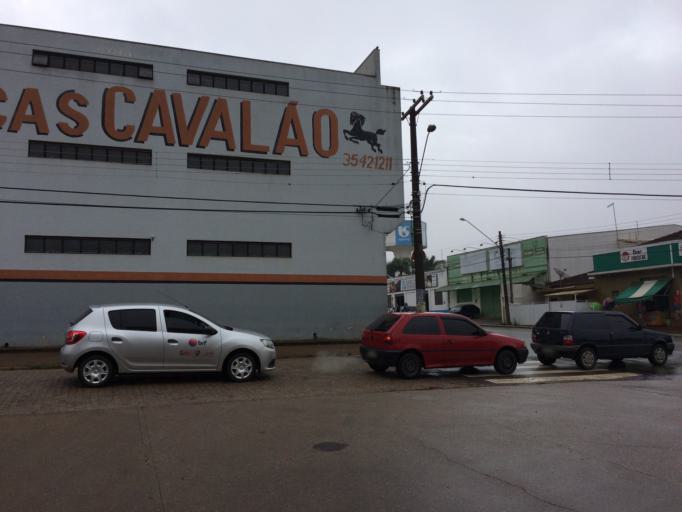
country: BR
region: Sao Paulo
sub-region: Capao Bonito
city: Capao Bonito
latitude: -24.0085
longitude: -48.3414
